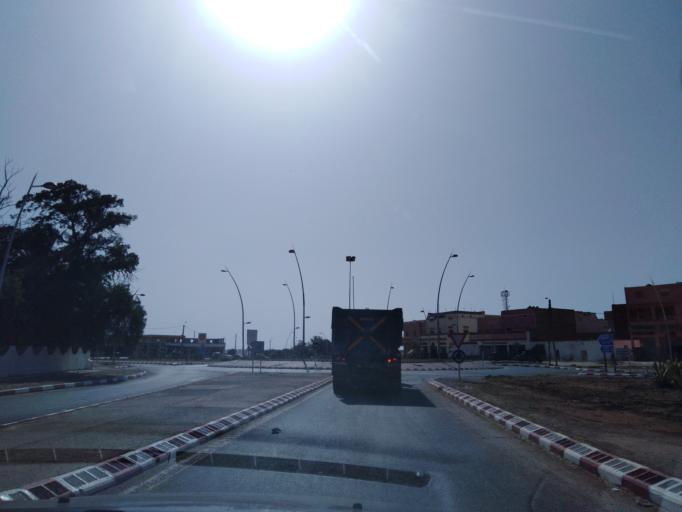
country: MA
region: Doukkala-Abda
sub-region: Safi
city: Safi
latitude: 32.2536
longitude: -8.9819
